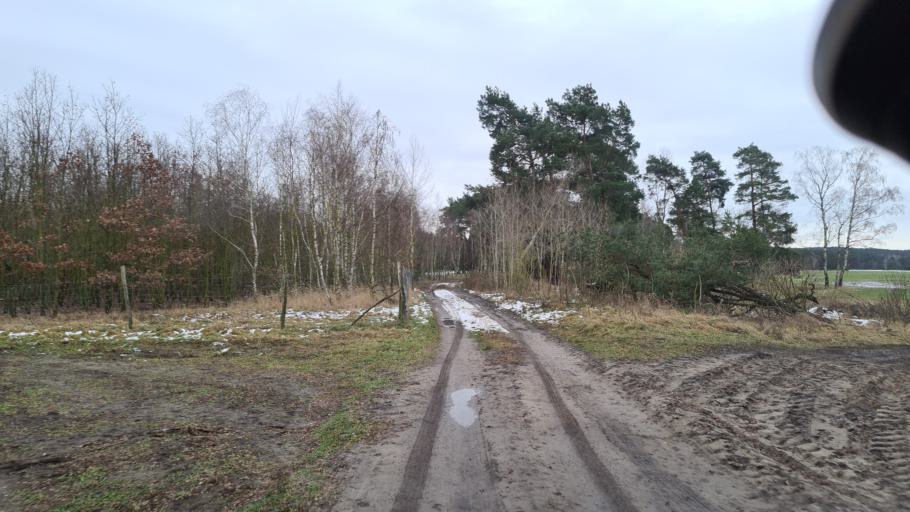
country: DE
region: Brandenburg
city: Schenkendobern
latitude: 51.9106
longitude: 14.5900
